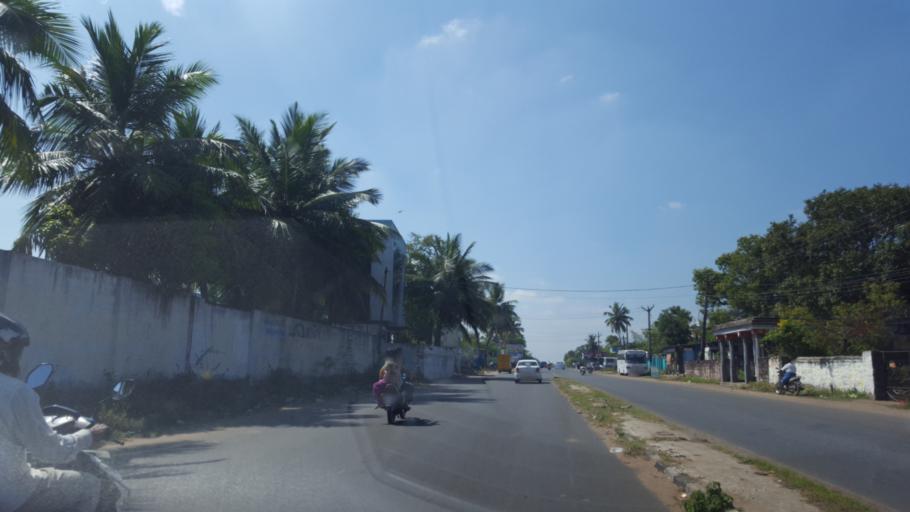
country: IN
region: Tamil Nadu
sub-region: Kancheepuram
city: Karumbakkam
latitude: 12.7163
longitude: 80.1882
